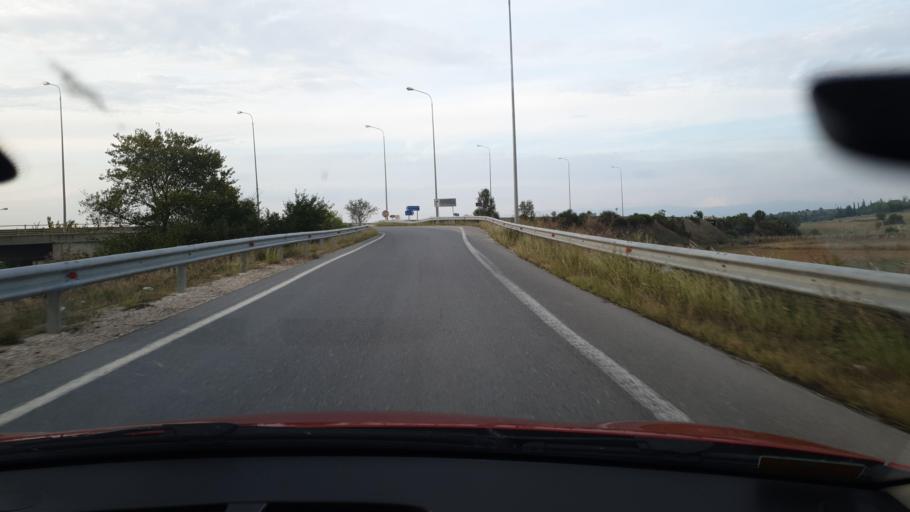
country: GR
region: Central Macedonia
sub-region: Nomos Kilkis
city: Kilkis
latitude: 41.0106
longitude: 22.8058
